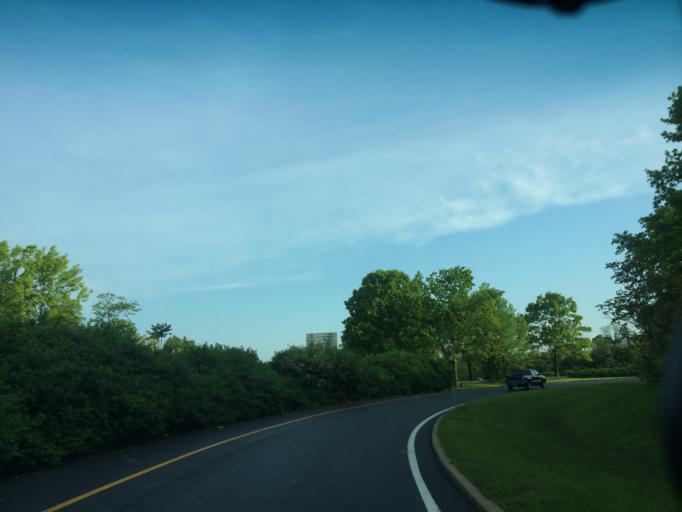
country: US
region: Maryland
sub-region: Carroll County
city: Mount Airy
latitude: 39.3577
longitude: -77.1691
